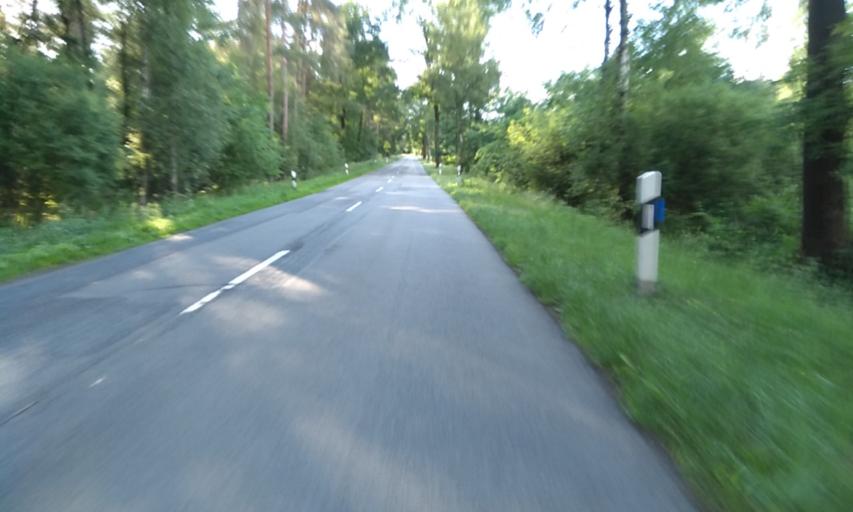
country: DE
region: Lower Saxony
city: Heeslingen
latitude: 53.3560
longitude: 9.3428
